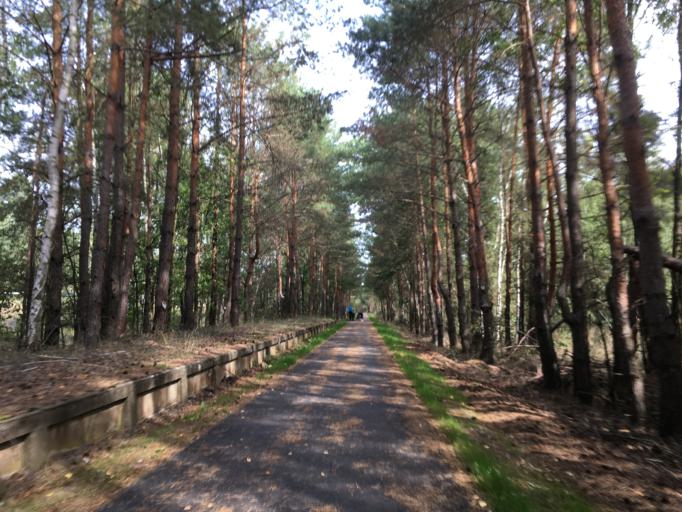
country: DE
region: Brandenburg
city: Heinersbruck
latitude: 51.8266
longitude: 14.5845
